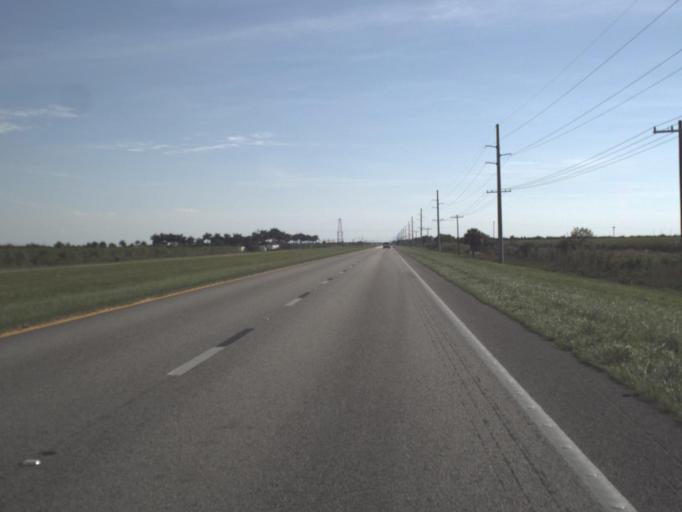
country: US
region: Florida
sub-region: Glades County
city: Moore Haven
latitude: 26.7875
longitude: -81.0829
